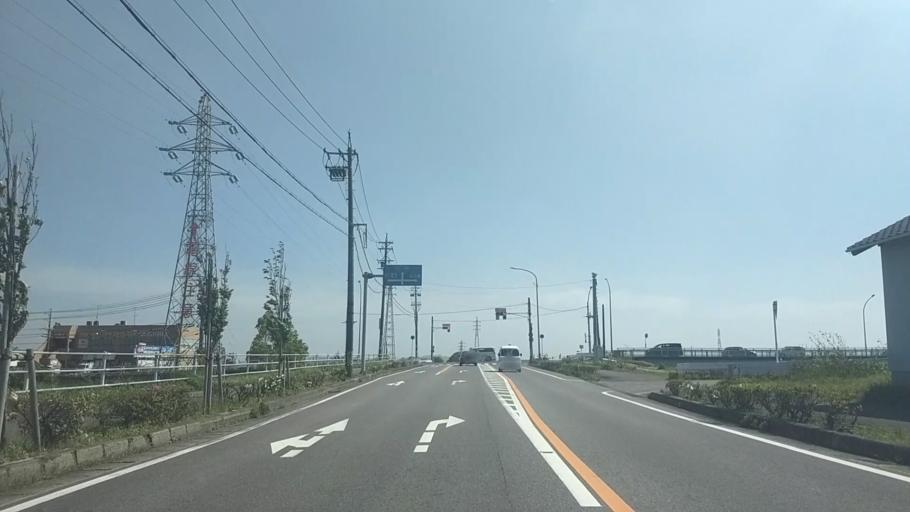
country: JP
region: Aichi
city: Okazaki
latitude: 34.9757
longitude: 137.1499
